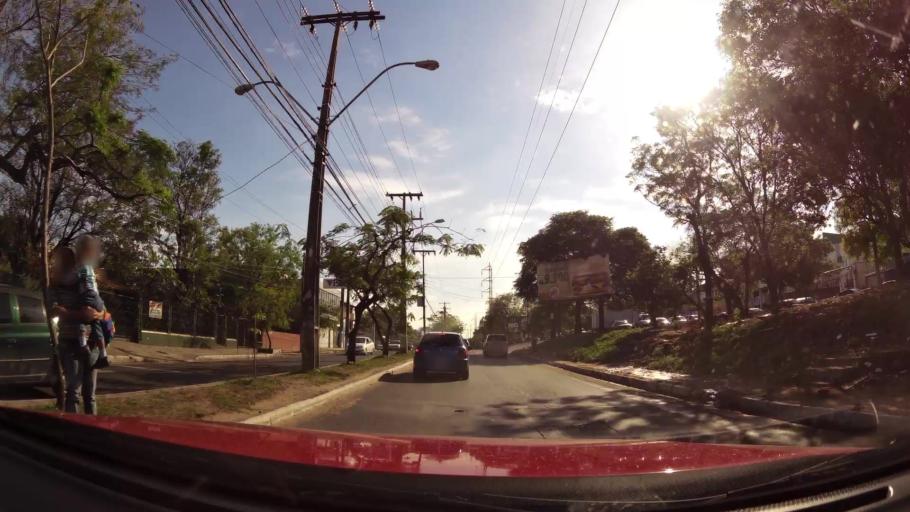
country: PY
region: Asuncion
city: Asuncion
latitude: -25.2673
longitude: -57.5987
